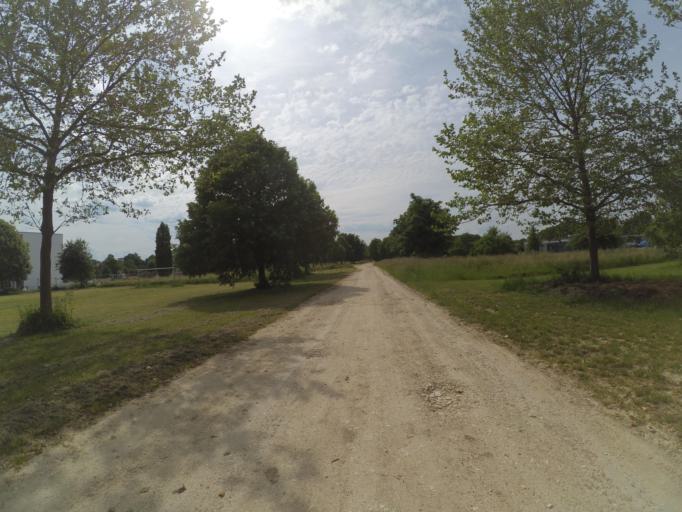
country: DE
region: Bavaria
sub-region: Swabia
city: Guenzburg
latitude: 48.4555
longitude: 10.2936
